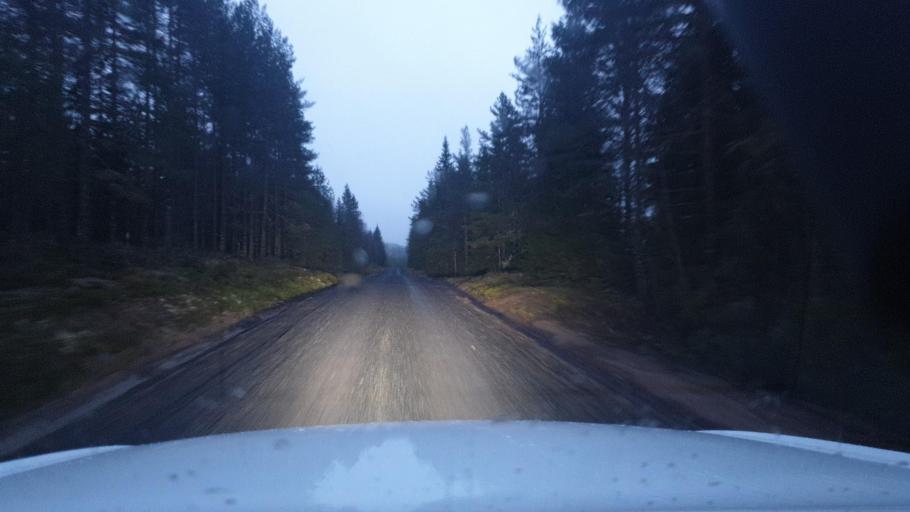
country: SE
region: Vaermland
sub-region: Eda Kommun
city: Charlottenberg
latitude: 60.1195
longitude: 12.6010
